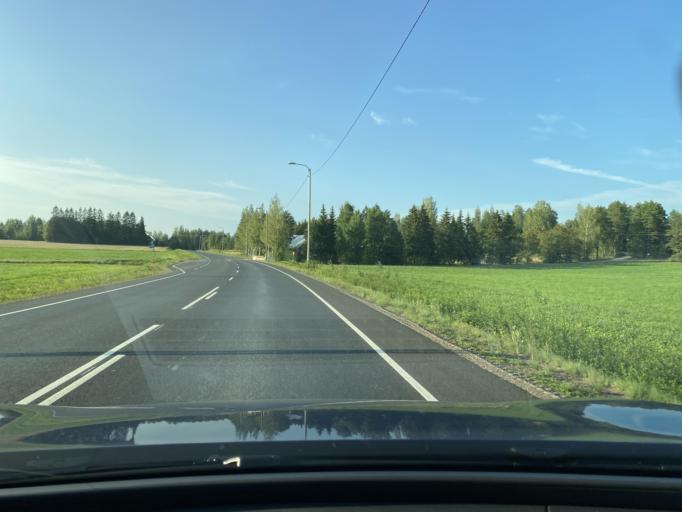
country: FI
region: Kymenlaakso
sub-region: Kouvola
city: Kouvola
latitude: 60.8766
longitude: 26.6032
